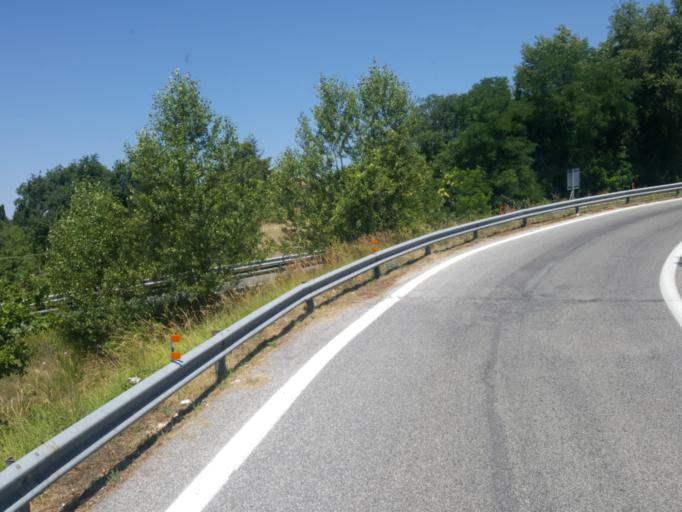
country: IT
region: The Marches
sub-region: Provincia di Macerata
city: Casette Verdini
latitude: 43.2342
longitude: 13.3687
